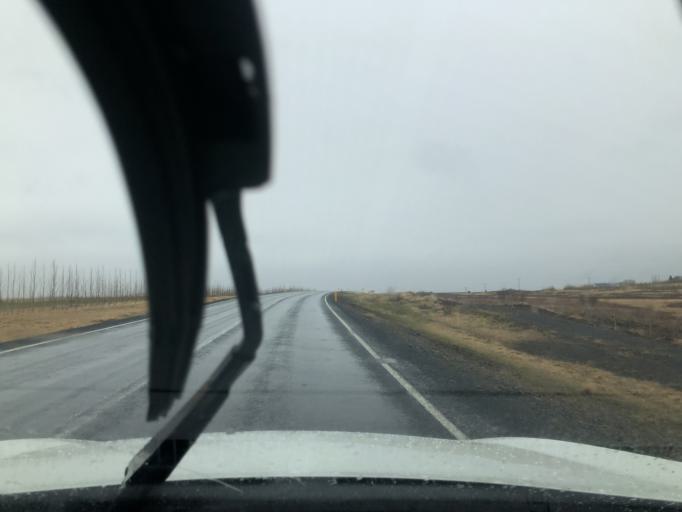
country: IS
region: South
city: Selfoss
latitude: 64.2770
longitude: -20.3495
